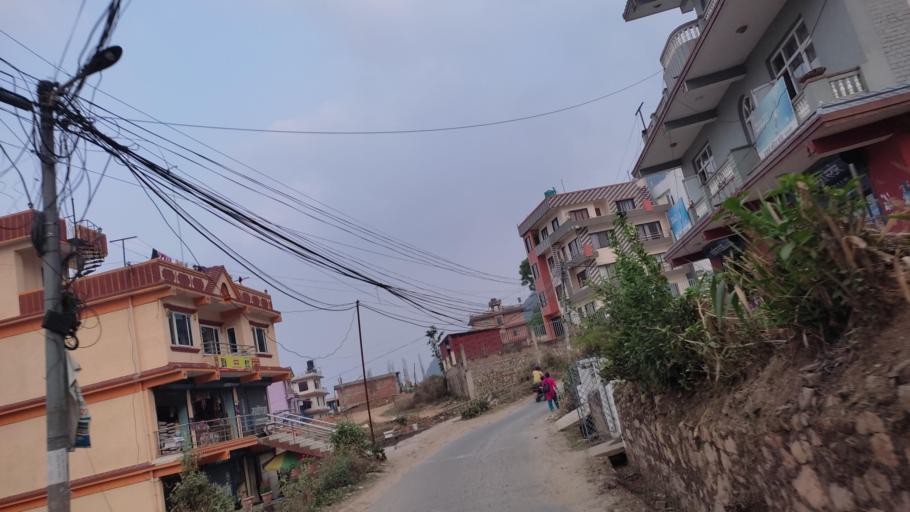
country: NP
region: Central Region
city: Kirtipur
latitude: 27.6636
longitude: 85.2541
